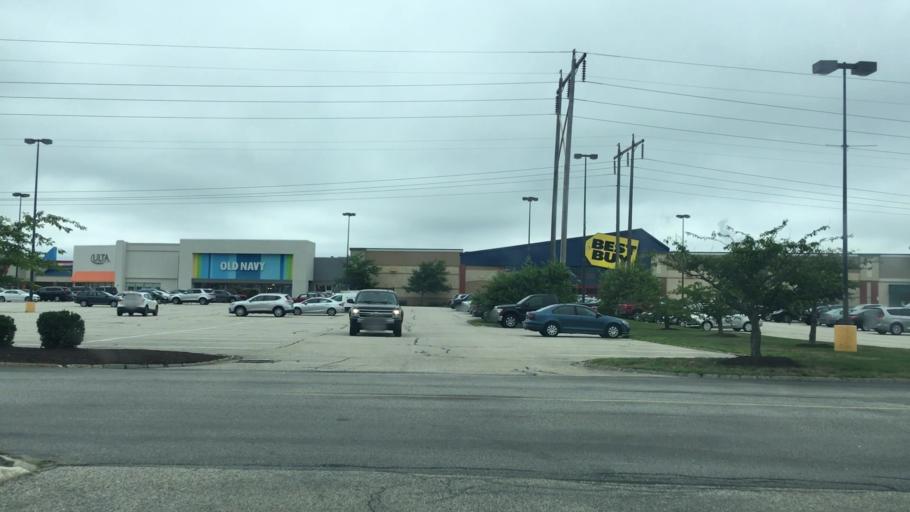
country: US
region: Maine
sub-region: York County
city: South Eliot
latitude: 43.0933
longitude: -70.7983
